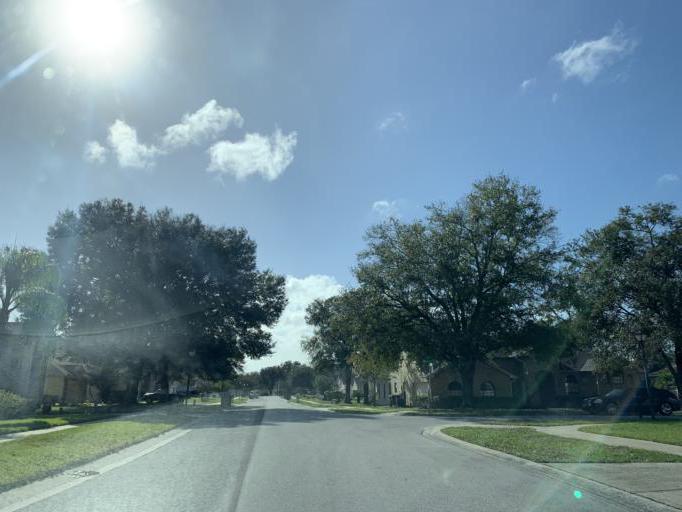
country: US
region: Florida
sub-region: Orange County
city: Clarcona
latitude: 28.6292
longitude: -81.4741
